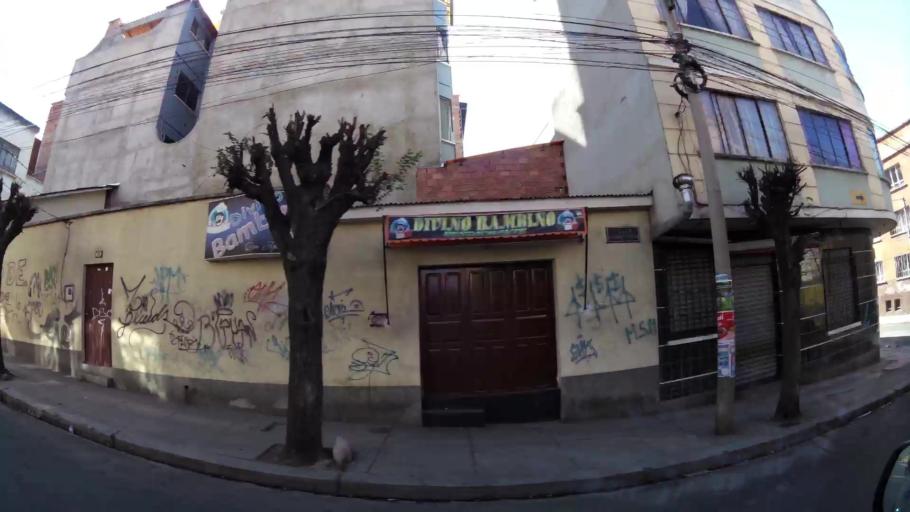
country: BO
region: La Paz
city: La Paz
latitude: -16.5048
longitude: -68.1360
